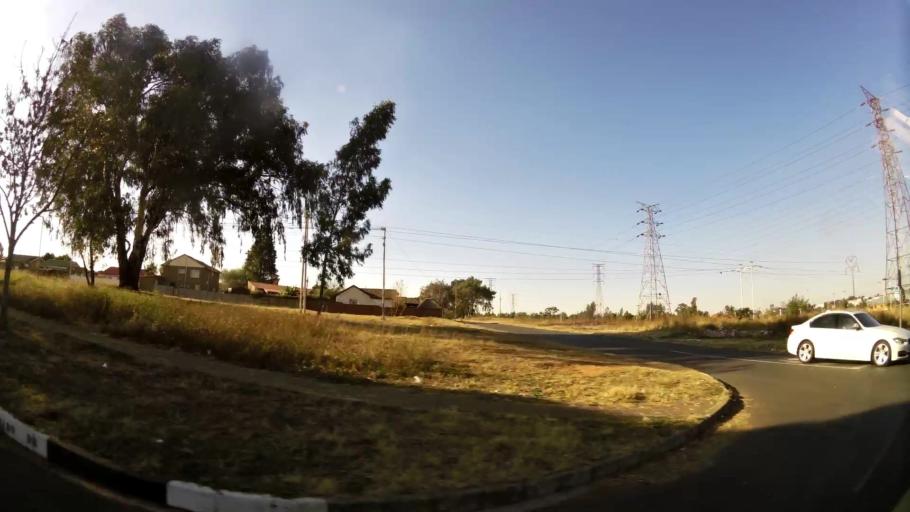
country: ZA
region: Gauteng
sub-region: City of Johannesburg Metropolitan Municipality
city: Johannesburg
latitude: -26.2160
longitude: 27.9829
